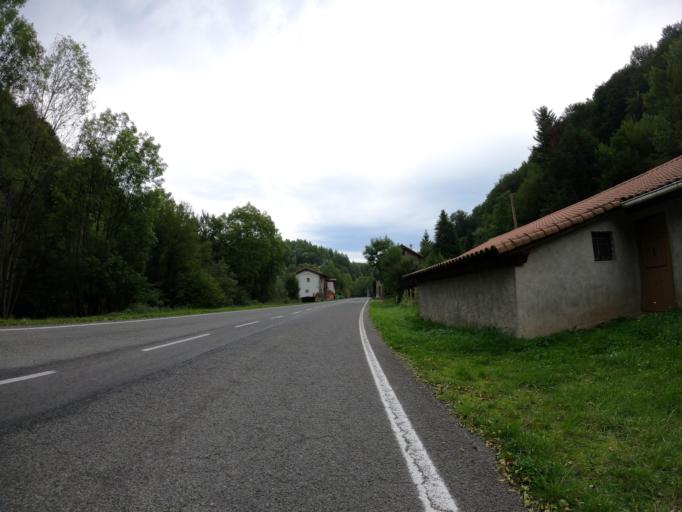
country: ES
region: Navarre
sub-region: Provincia de Navarra
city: Lekunberri
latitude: 43.0295
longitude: -1.9062
